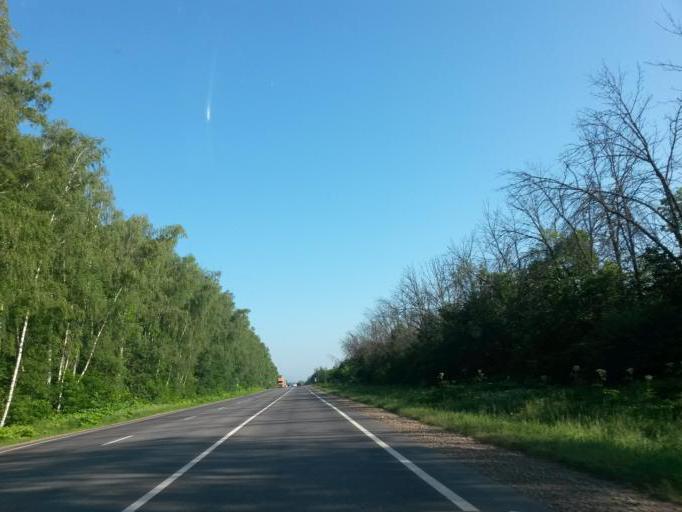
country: RU
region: Moskovskaya
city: Barybino
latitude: 55.2407
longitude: 37.8559
